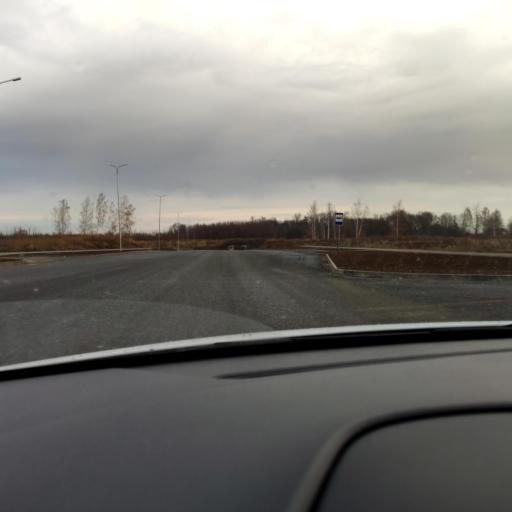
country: RU
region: Tatarstan
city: Osinovo
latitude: 55.8618
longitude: 48.8983
